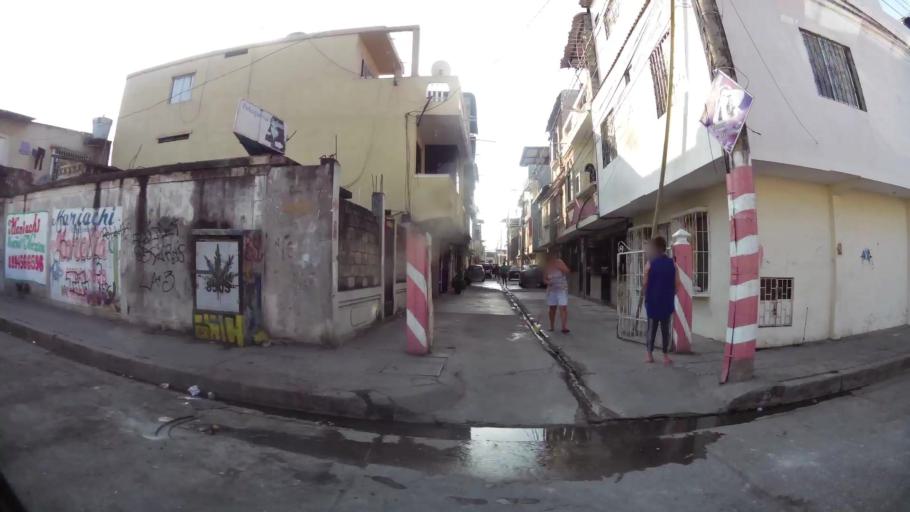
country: EC
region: Guayas
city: Eloy Alfaro
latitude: -2.1811
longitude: -79.8560
